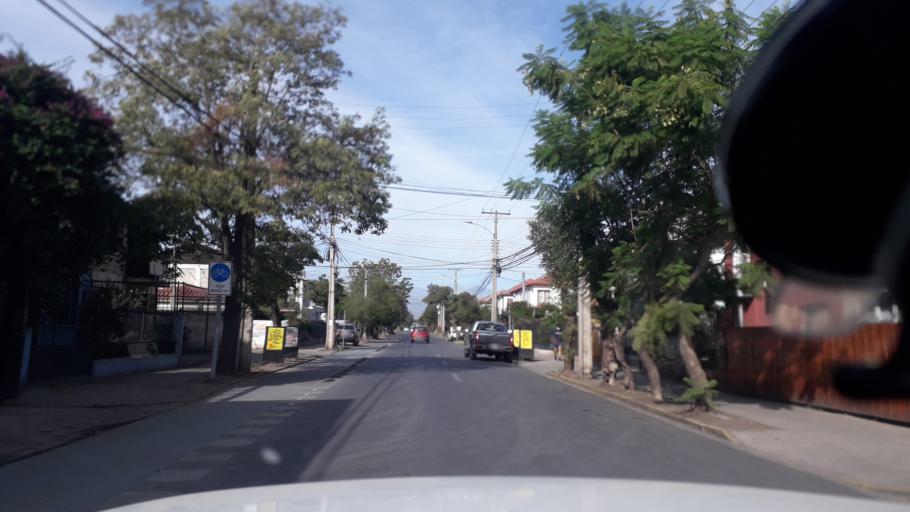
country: CL
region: Valparaiso
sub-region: Provincia de San Felipe
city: San Felipe
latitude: -32.7516
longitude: -70.7193
